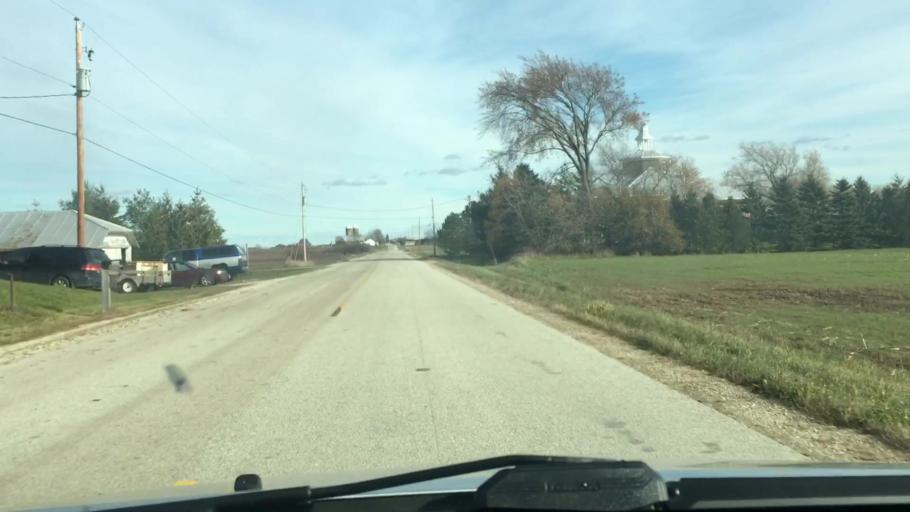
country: US
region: Wisconsin
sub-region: Kewaunee County
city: Luxemburg
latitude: 44.6976
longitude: -87.6113
